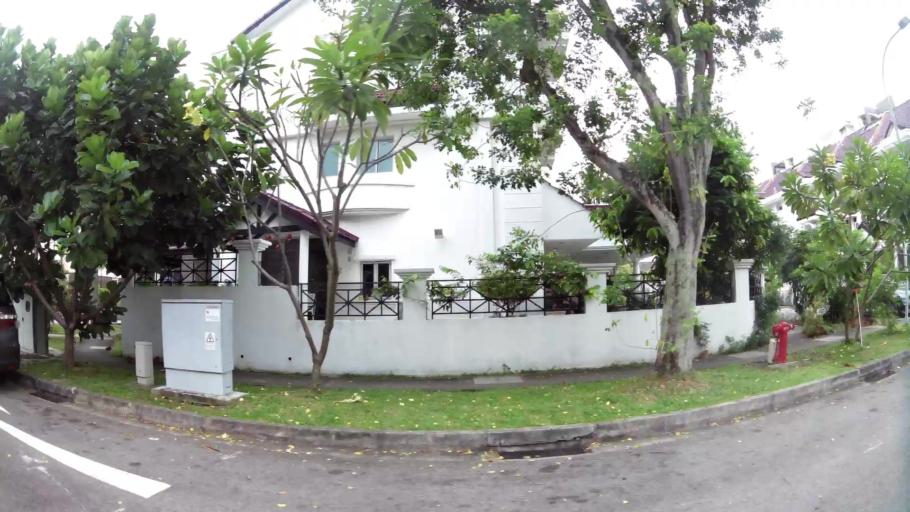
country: SG
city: Singapore
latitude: 1.3567
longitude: 103.8773
